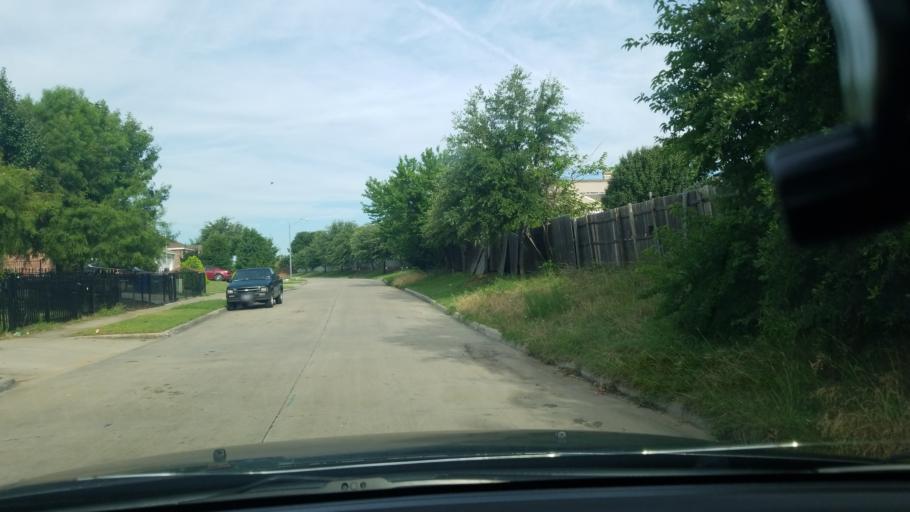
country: US
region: Texas
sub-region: Dallas County
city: Balch Springs
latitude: 32.7596
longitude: -96.6539
